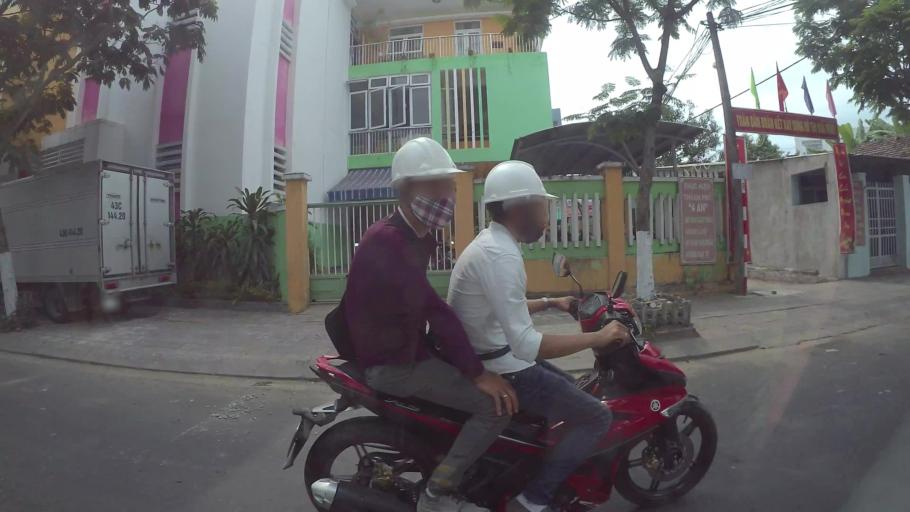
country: VN
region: Da Nang
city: Cam Le
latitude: 16.0369
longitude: 108.1841
